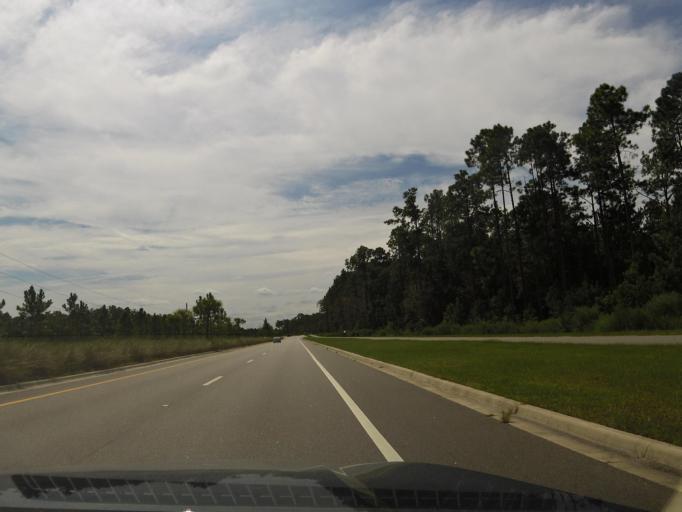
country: US
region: Florida
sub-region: Saint Johns County
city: Fruit Cove
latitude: 30.0449
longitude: -81.5297
